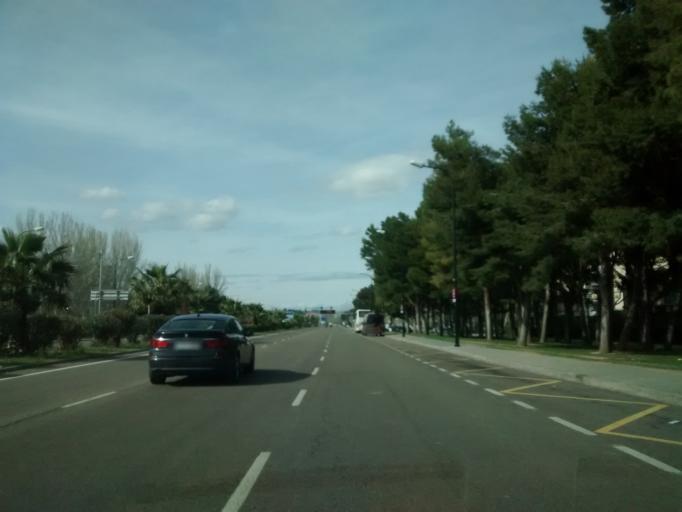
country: ES
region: Aragon
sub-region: Provincia de Zaragoza
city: Zaragoza
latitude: 41.6619
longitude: -0.8809
